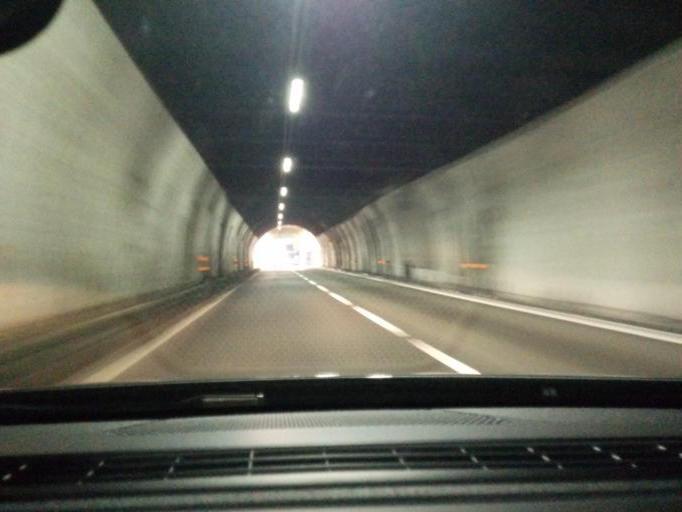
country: IT
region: Liguria
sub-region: Provincia di Genova
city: San Teodoro
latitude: 44.4296
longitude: 8.8316
